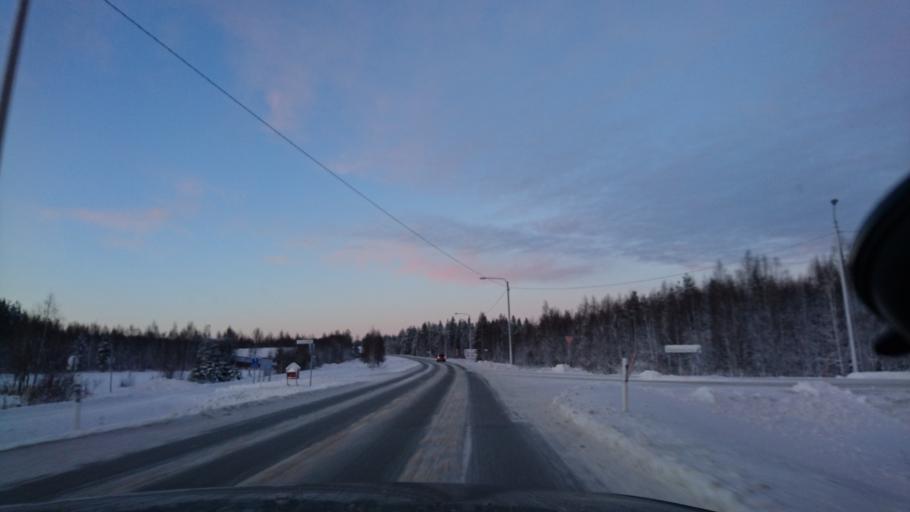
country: FI
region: Lapland
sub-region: Rovaniemi
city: Ranua
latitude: 65.9369
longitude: 26.4900
